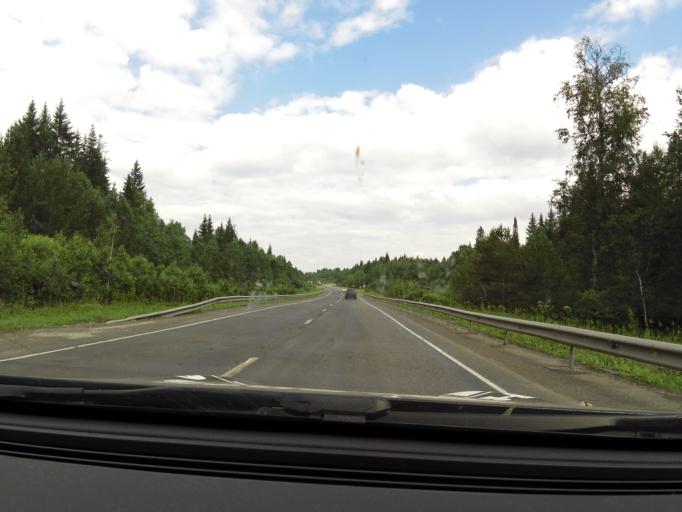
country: RU
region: Sverdlovsk
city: Druzhinino
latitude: 56.7973
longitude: 59.4492
